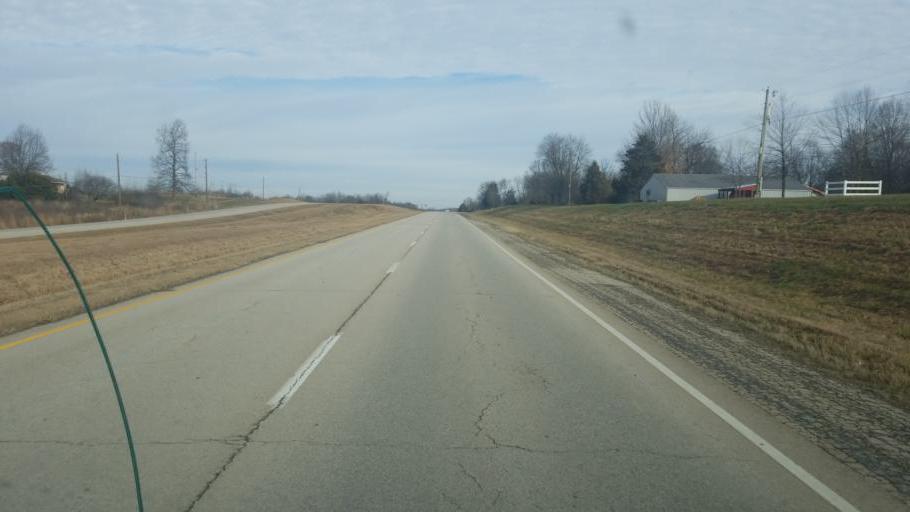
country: US
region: Missouri
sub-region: Stoddard County
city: Bloomfield
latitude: 36.8484
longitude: -89.9403
